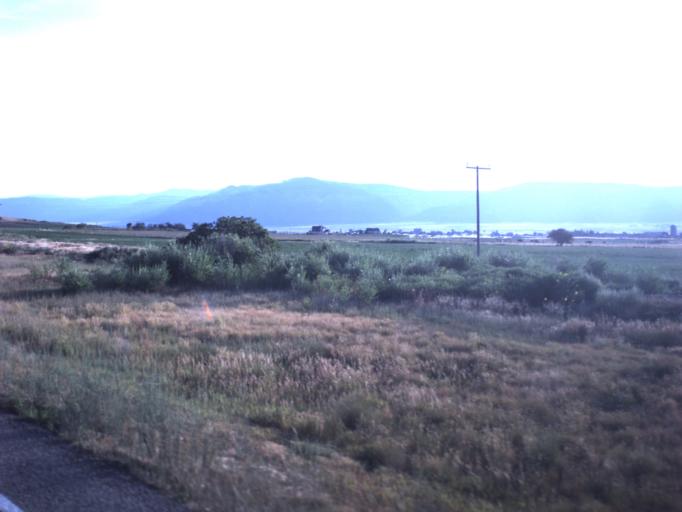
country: US
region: Utah
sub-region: Sanpete County
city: Moroni
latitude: 39.4851
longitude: -111.5185
